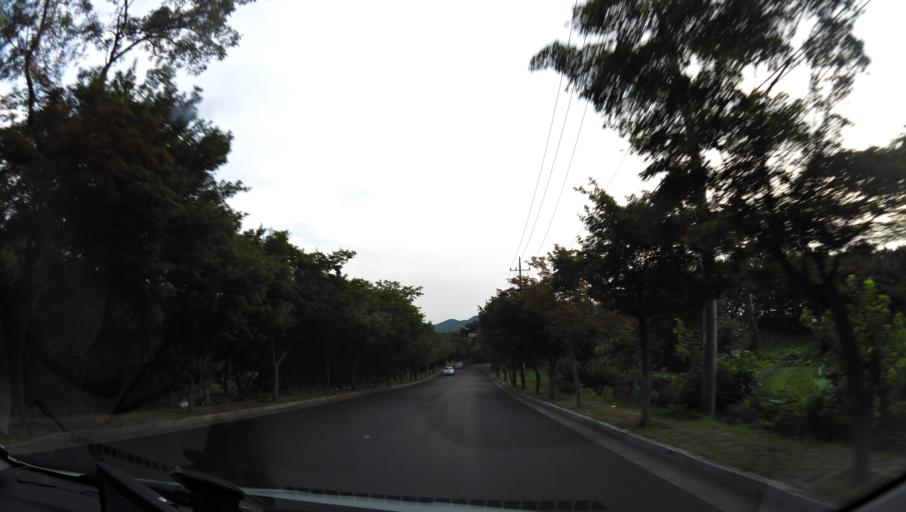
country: KR
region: Daegu
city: Daegu
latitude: 35.9865
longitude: 128.6466
